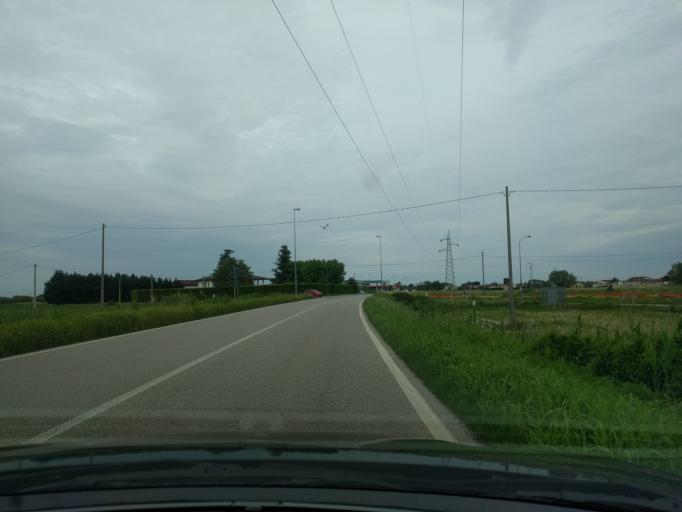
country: IT
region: Veneto
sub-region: Provincia di Rovigo
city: Sant'Apollinare
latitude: 45.0441
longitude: 11.8200
